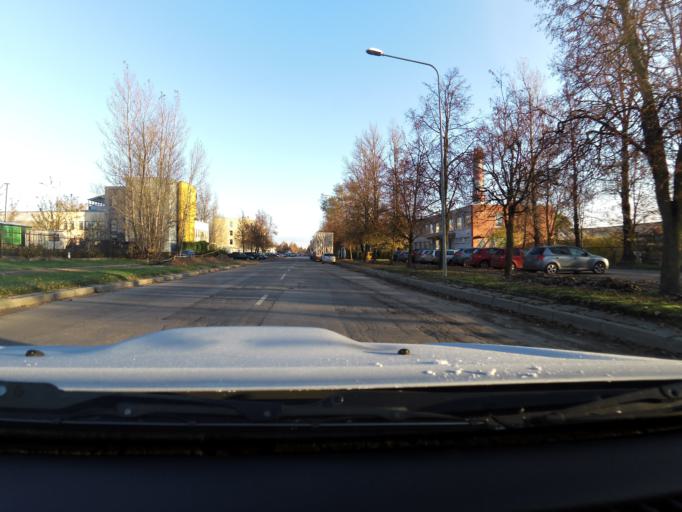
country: LT
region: Vilnius County
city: Vilkpede
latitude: 54.6324
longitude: 25.2653
